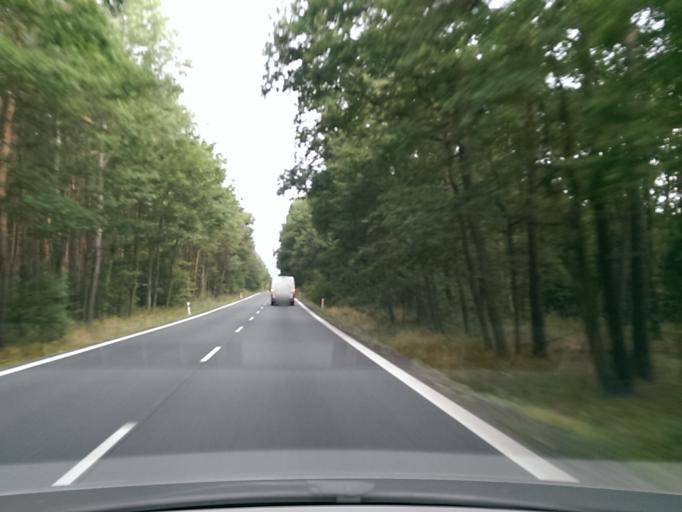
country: CZ
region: Central Bohemia
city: Loucen
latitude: 50.2613
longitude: 14.9787
